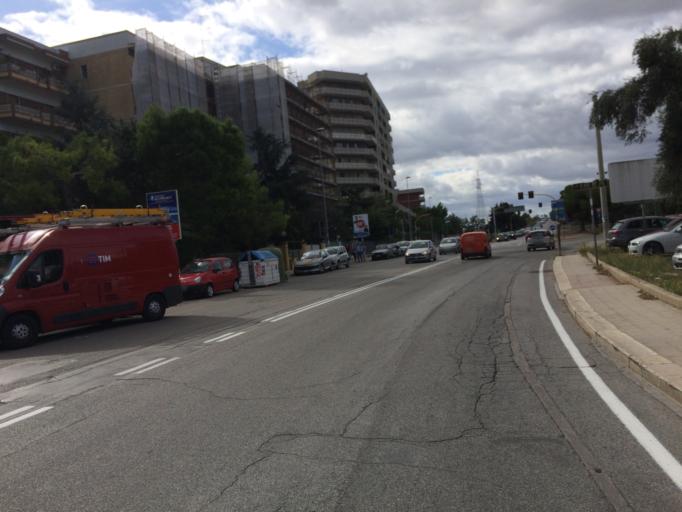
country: IT
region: Apulia
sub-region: Provincia di Bari
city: Bari
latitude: 41.0944
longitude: 16.8546
